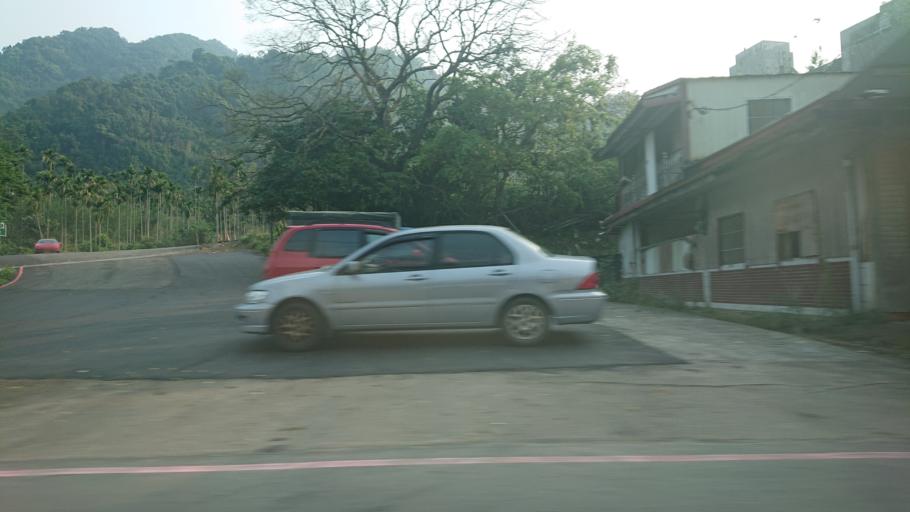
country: TW
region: Taiwan
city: Daxi
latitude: 24.8712
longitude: 121.4059
